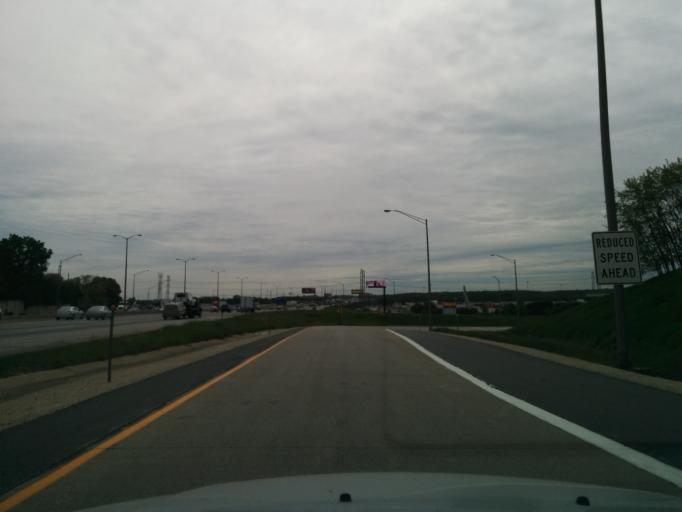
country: US
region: Illinois
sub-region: Cook County
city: Willow Springs
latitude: 41.7561
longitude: -87.8788
